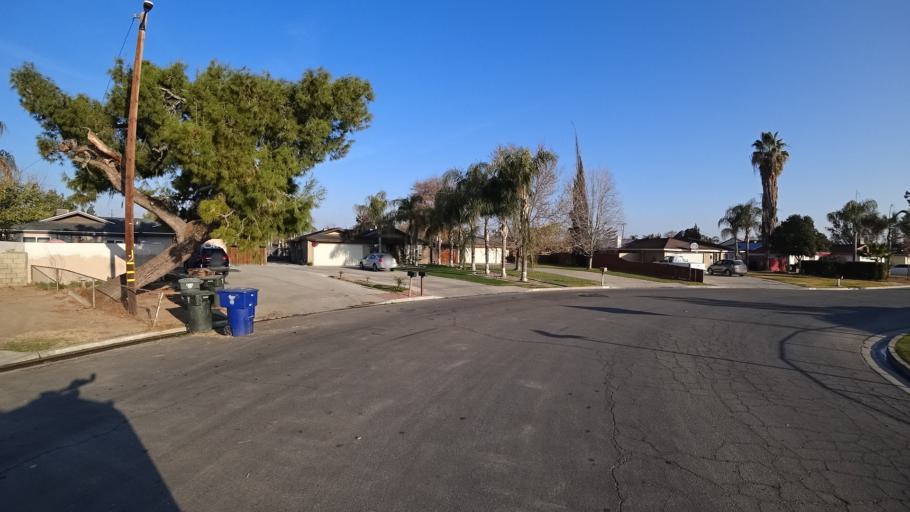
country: US
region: California
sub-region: Kern County
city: Greenfield
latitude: 35.2985
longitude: -119.0199
